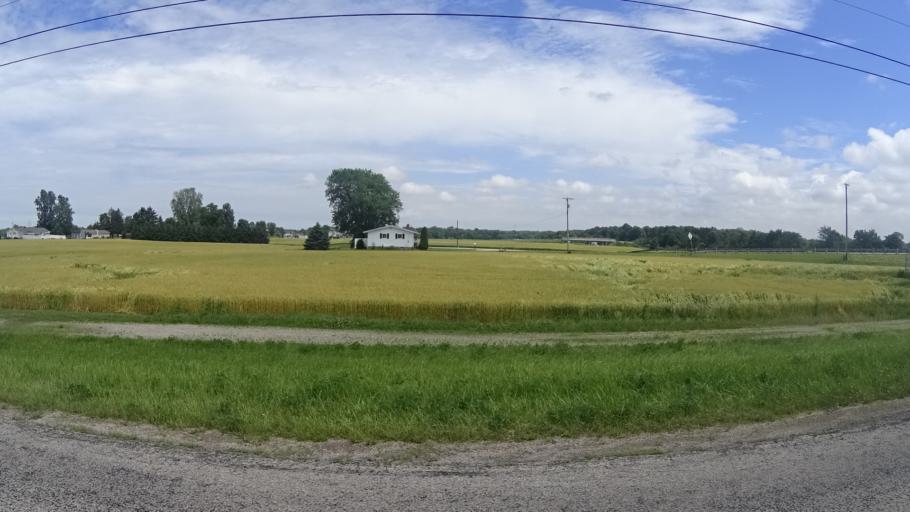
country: US
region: Ohio
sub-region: Erie County
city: Milan
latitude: 41.3270
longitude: -82.5435
